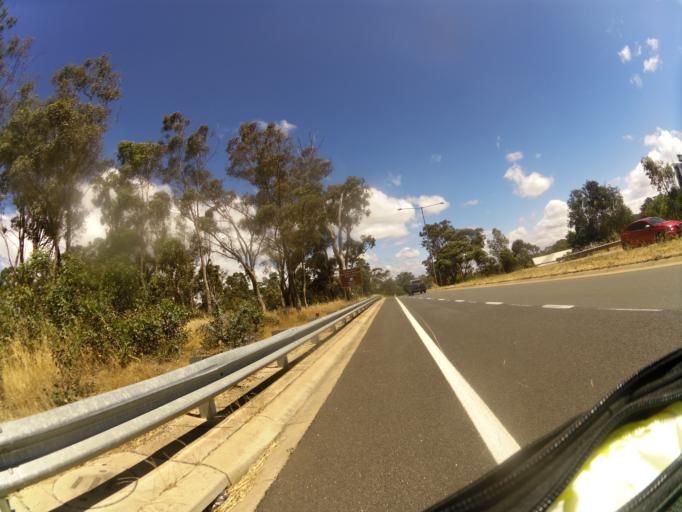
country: AU
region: Victoria
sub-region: Mount Alexander
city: Castlemaine
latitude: -37.0066
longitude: 144.2477
